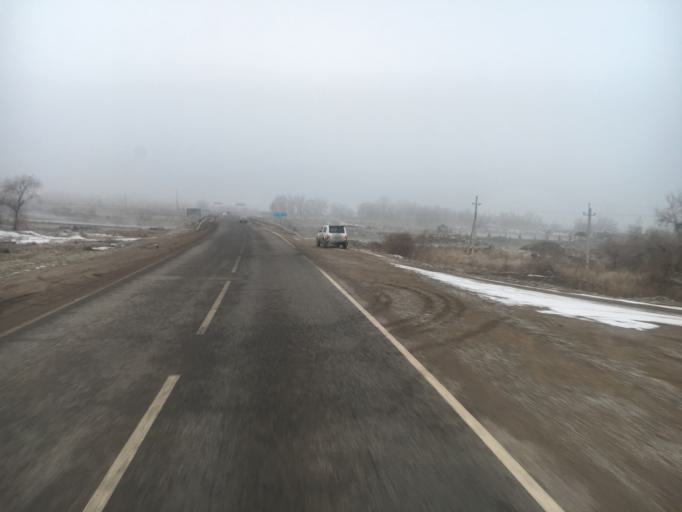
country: KZ
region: Zhambyl
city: Sarykemer
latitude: 43.0400
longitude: 71.5385
